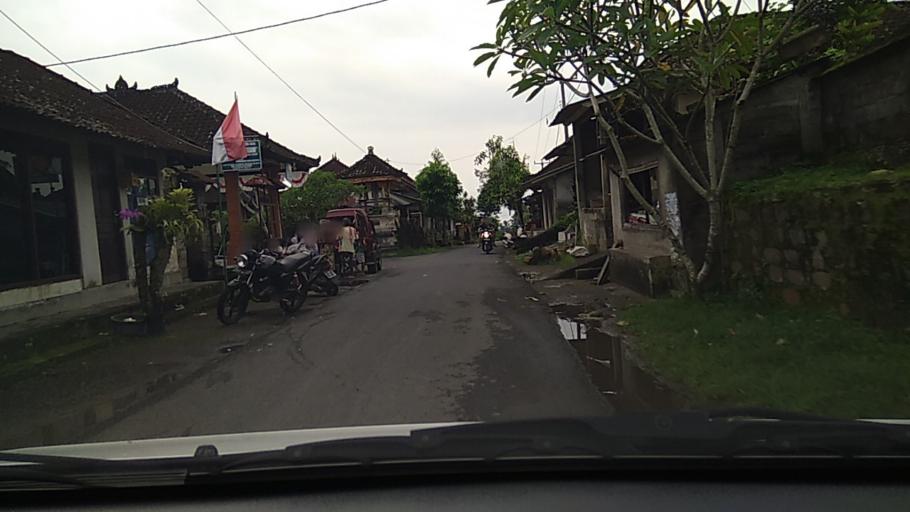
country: ID
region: Bali
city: Banjar Dujung Kaja
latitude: -8.4155
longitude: 115.2828
